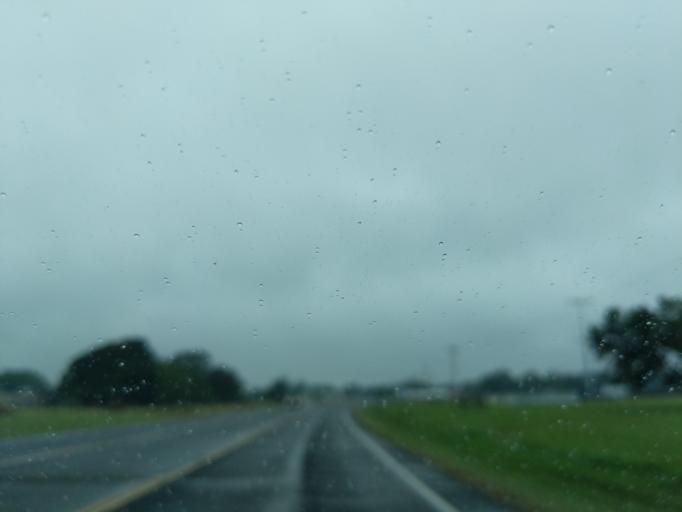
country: US
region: Louisiana
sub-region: Vermilion Parish
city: Kaplan
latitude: 29.9937
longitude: -92.2717
